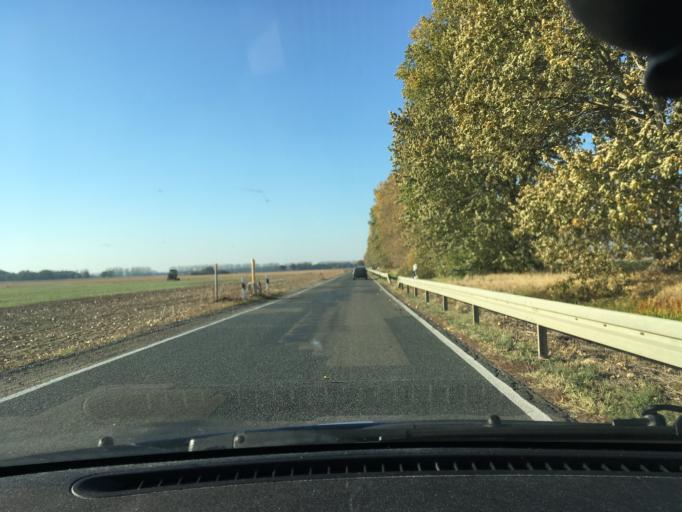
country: DE
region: Mecklenburg-Vorpommern
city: Domitz
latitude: 53.1522
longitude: 11.2538
